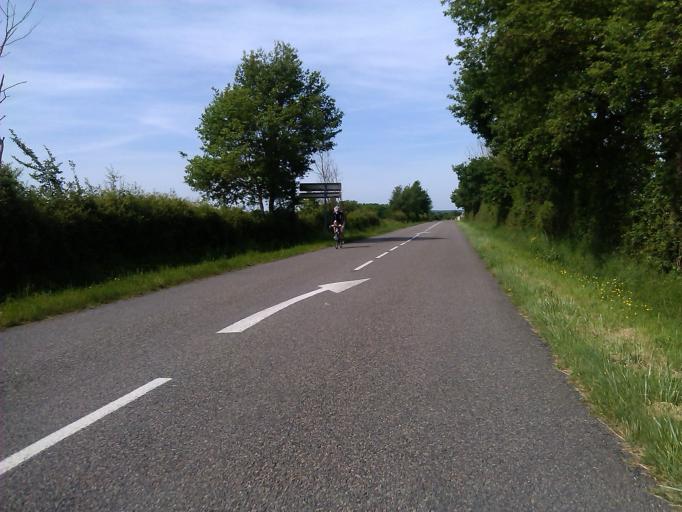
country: FR
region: Auvergne
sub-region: Departement de l'Allier
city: Dompierre-sur-Besbre
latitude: 46.5288
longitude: 3.6181
